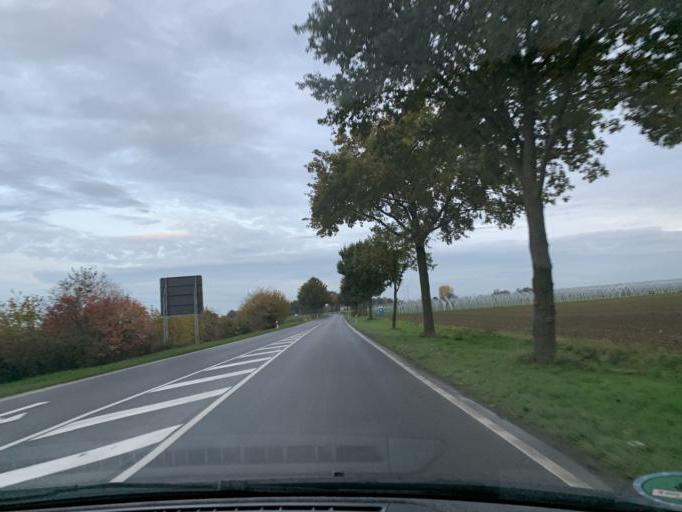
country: DE
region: North Rhine-Westphalia
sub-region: Regierungsbezirk Koln
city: Titz
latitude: 51.0080
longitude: 6.4007
